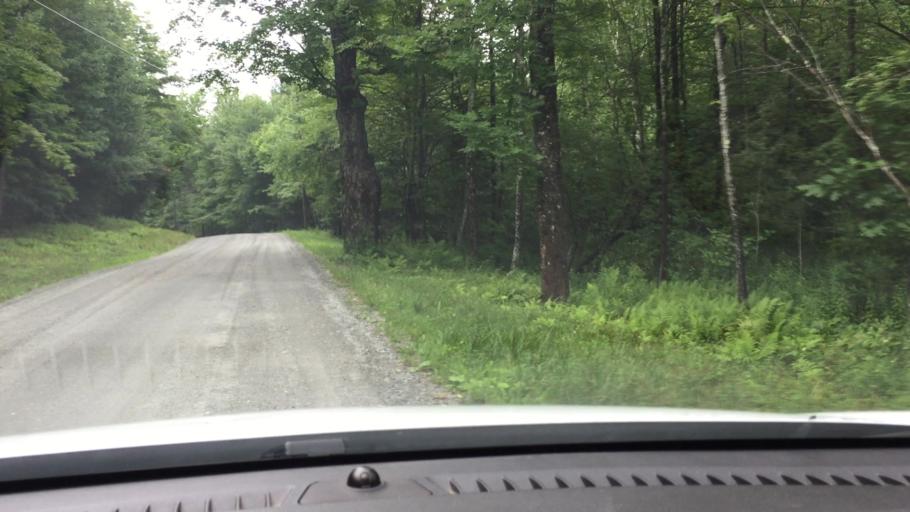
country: US
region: Massachusetts
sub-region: Berkshire County
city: Hinsdale
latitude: 42.4119
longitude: -73.0557
